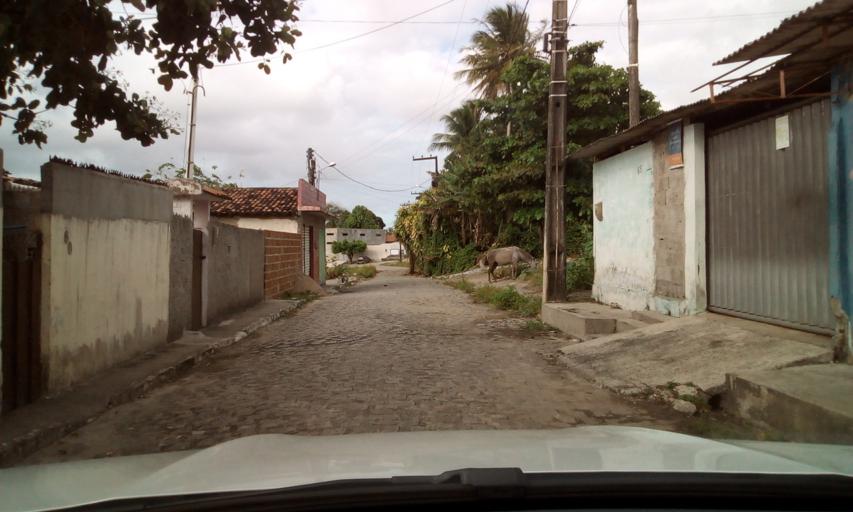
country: BR
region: Paraiba
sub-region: Joao Pessoa
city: Joao Pessoa
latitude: -7.1497
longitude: -34.8835
